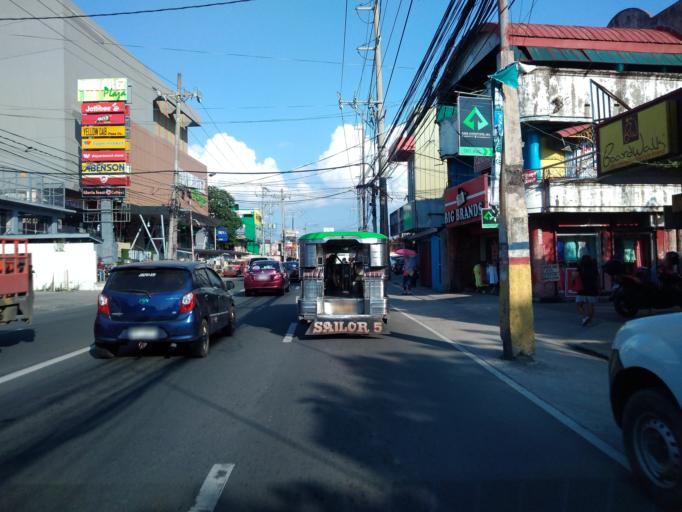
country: PH
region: Calabarzon
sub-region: Province of Laguna
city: Los Banos
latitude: 14.1790
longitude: 121.2384
